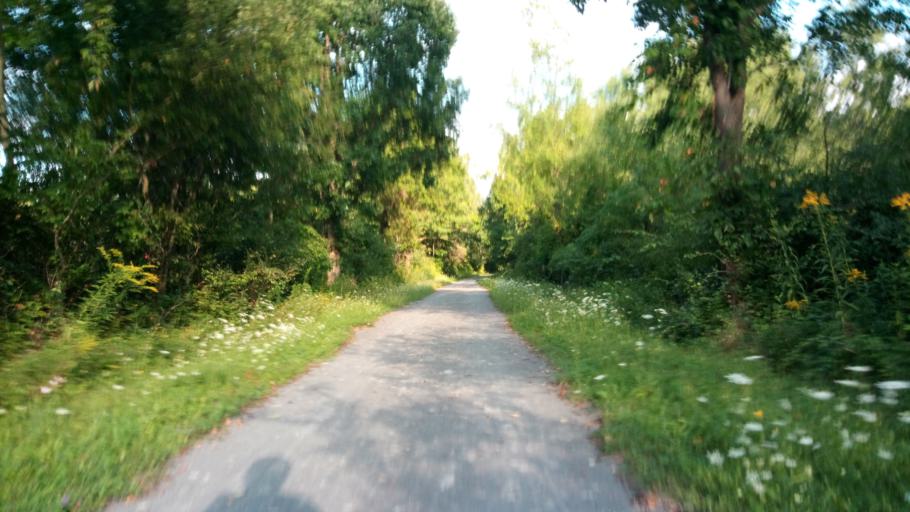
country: US
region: New York
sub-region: Ontario County
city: Victor
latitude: 43.0004
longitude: -77.4461
